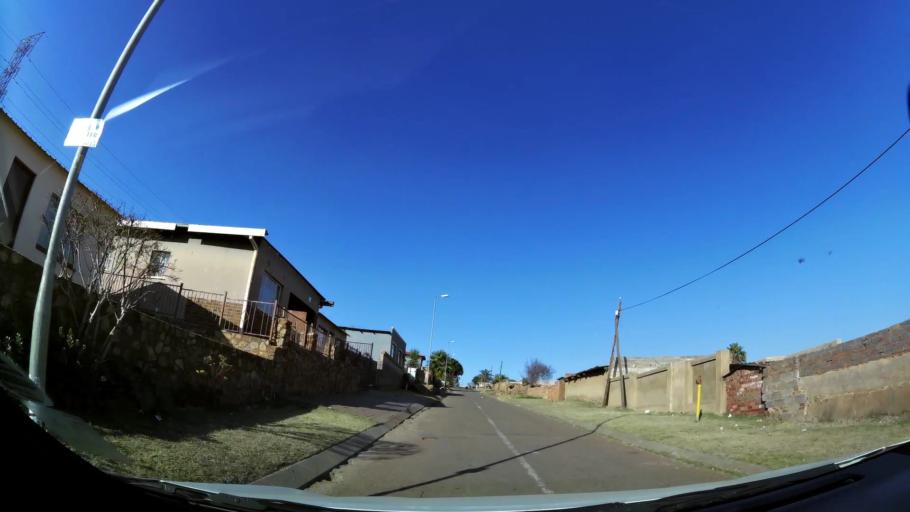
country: ZA
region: Gauteng
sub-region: City of Tshwane Metropolitan Municipality
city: Cullinan
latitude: -25.7022
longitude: 28.3716
